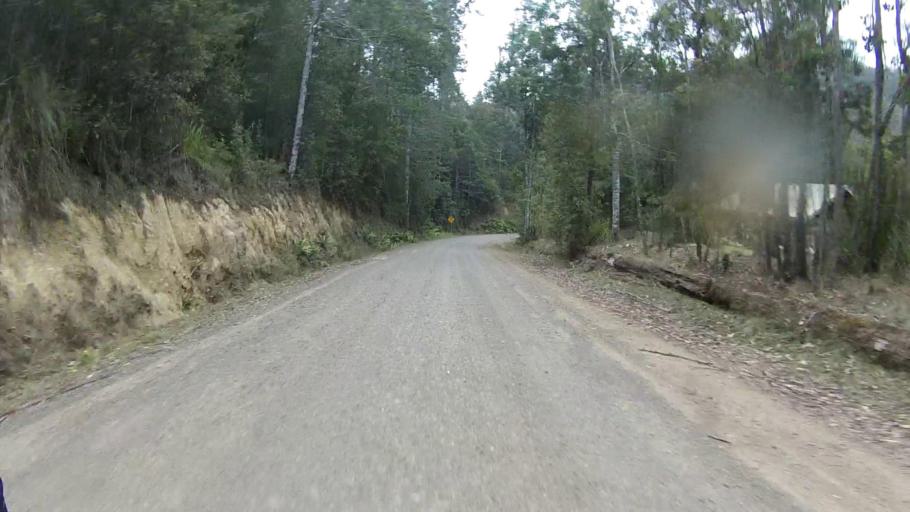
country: AU
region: Tasmania
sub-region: Sorell
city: Sorell
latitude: -42.7073
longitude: 147.8455
